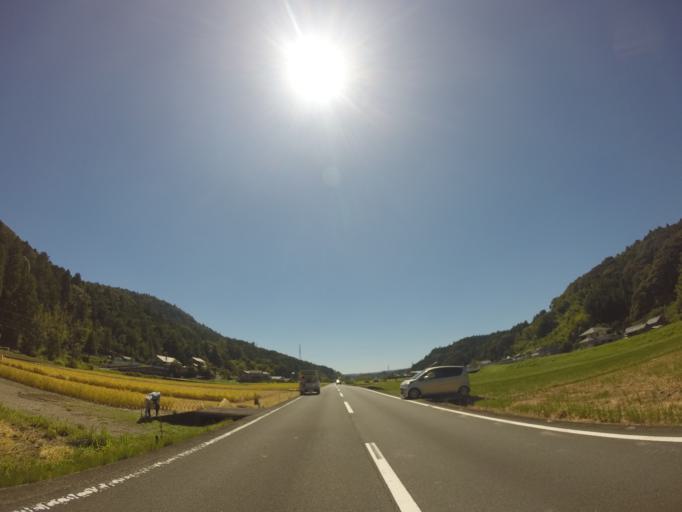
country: JP
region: Shizuoka
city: Kanaya
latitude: 34.8697
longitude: 138.1335
